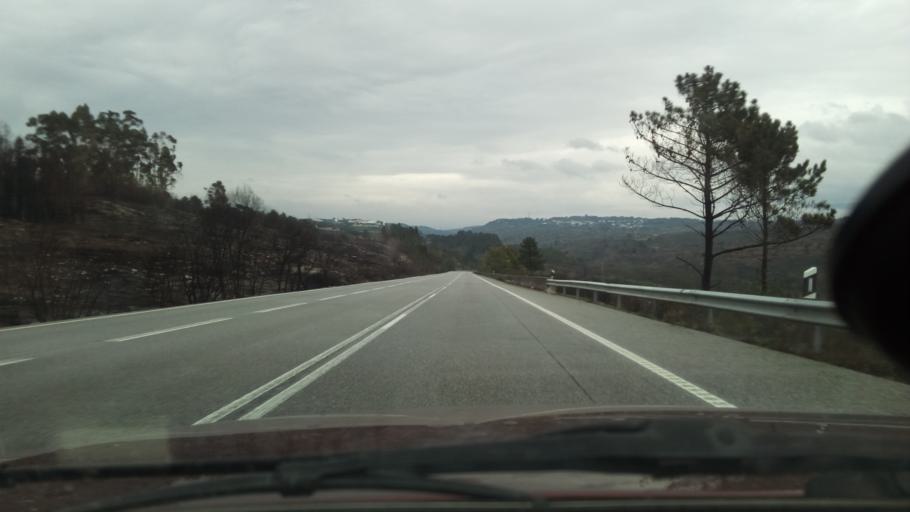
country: PT
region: Guarda
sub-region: Fornos de Algodres
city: Fornos de Algodres
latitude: 40.6022
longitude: -7.5525
